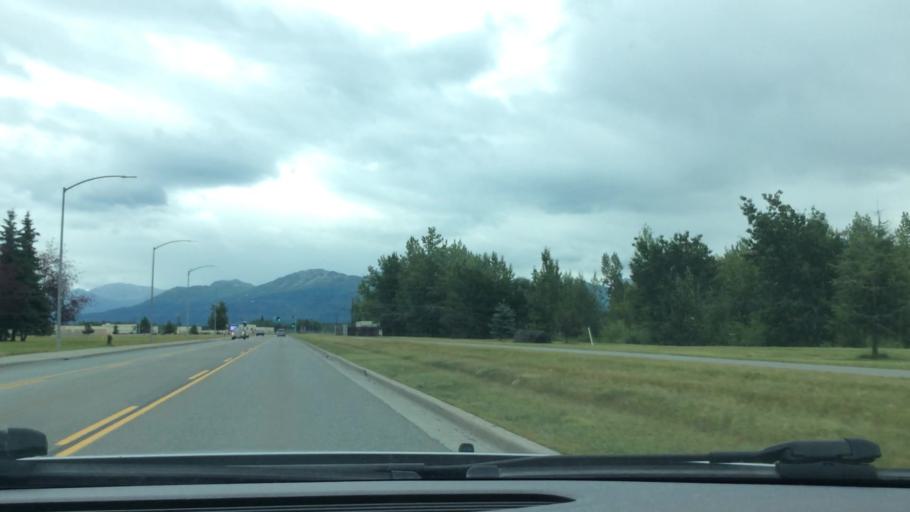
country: US
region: Alaska
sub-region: Anchorage Municipality
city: Anchorage
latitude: 61.2391
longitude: -149.8069
